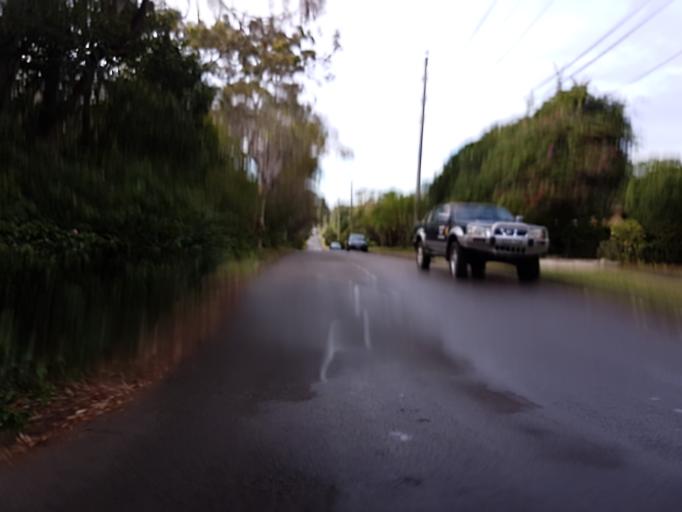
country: AU
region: New South Wales
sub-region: Warringah
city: Allambie Heights
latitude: -33.7576
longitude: 151.2319
